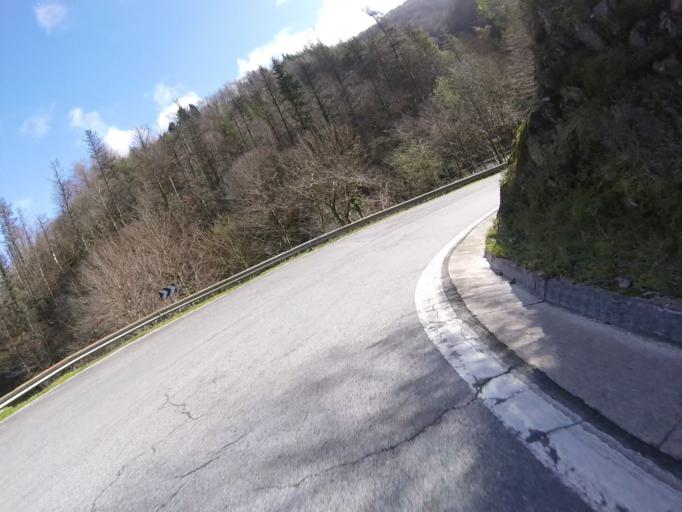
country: ES
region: Navarre
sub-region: Provincia de Navarra
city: Ezkurra
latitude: 43.1065
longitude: -1.8581
